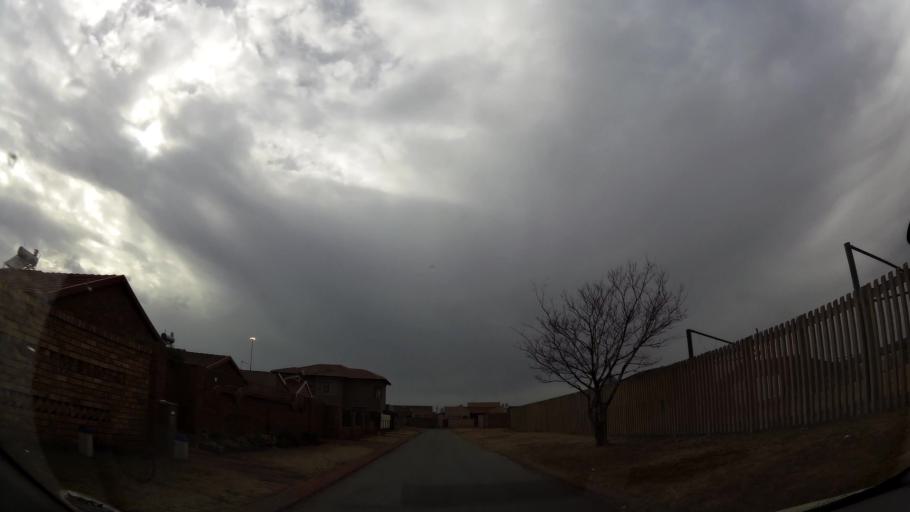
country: ZA
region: Gauteng
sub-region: Ekurhuleni Metropolitan Municipality
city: Germiston
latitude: -26.3258
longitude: 28.1940
